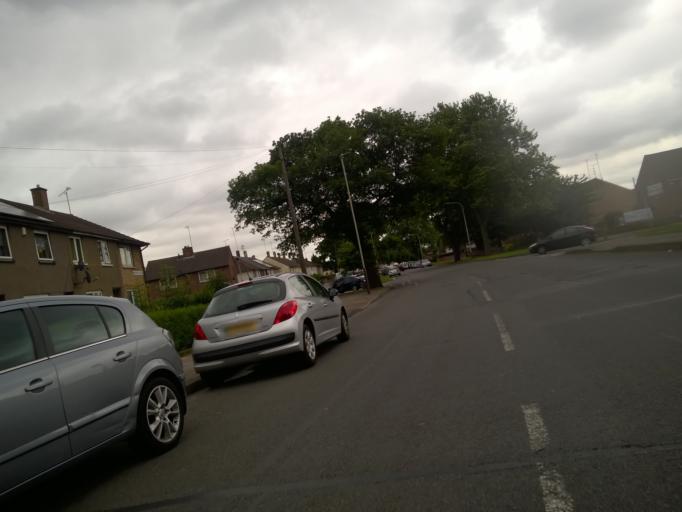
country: GB
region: England
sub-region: City of Leicester
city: Leicester
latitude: 52.6593
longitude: -1.1451
